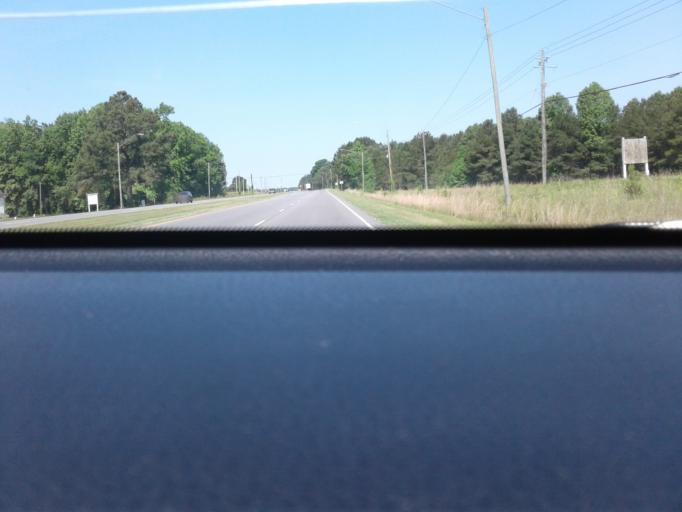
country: US
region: North Carolina
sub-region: Harnett County
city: Lillington
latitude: 35.4096
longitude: -78.7772
